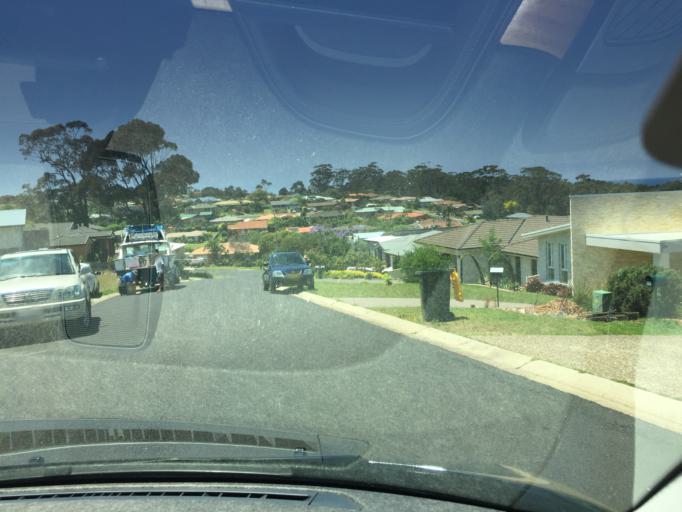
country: AU
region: New South Wales
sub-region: Bega Valley
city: Merimbula
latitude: -36.8538
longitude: 149.9304
